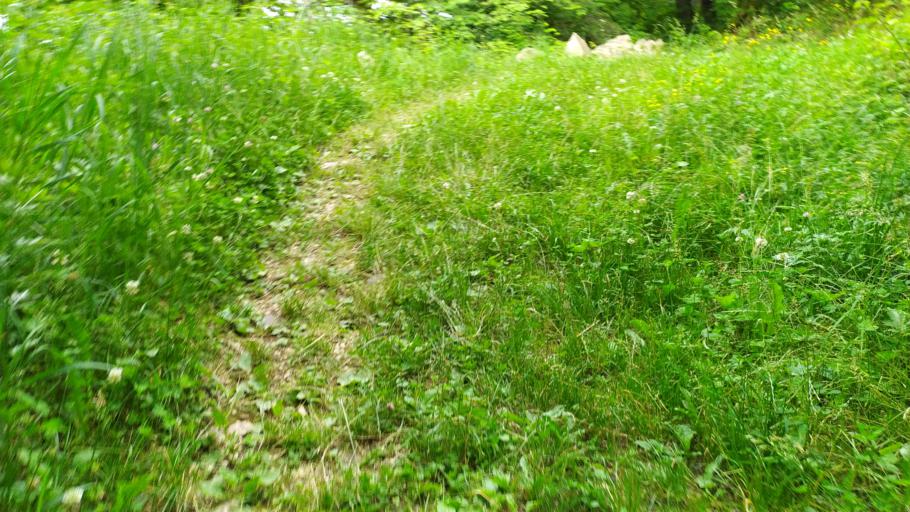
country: IT
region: Veneto
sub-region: Provincia di Vicenza
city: Torrebelvicino
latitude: 45.6871
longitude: 11.3144
